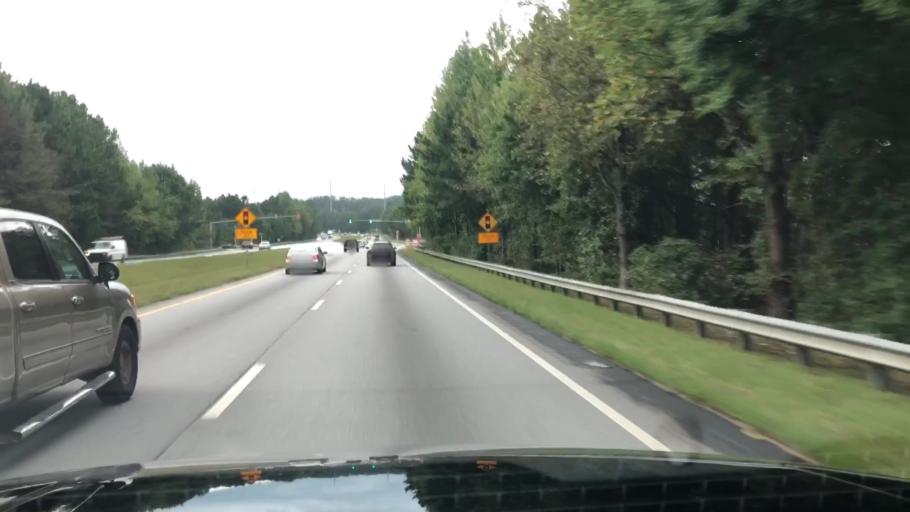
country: US
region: Georgia
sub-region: Cobb County
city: Mableton
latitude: 33.7507
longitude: -84.5900
